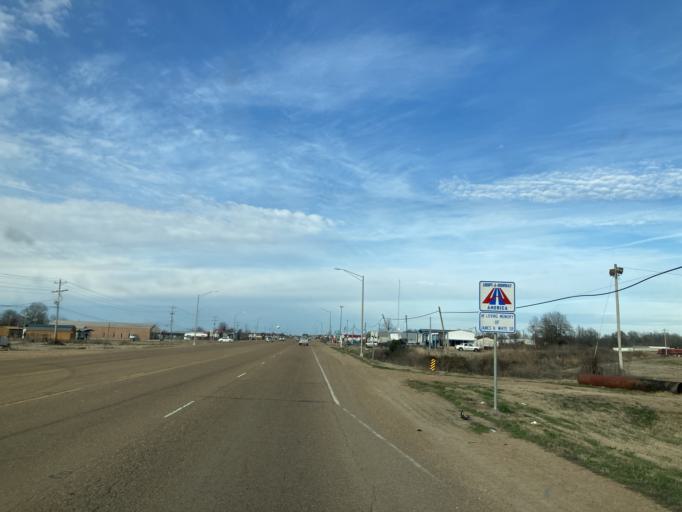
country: US
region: Mississippi
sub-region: Humphreys County
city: Belzoni
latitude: 33.1682
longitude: -90.4985
